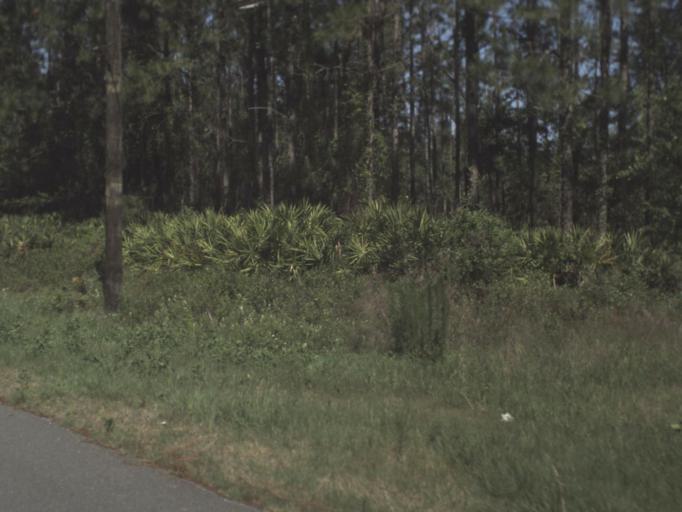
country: US
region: Florida
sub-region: Baker County
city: Macclenny
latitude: 30.2905
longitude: -82.0740
